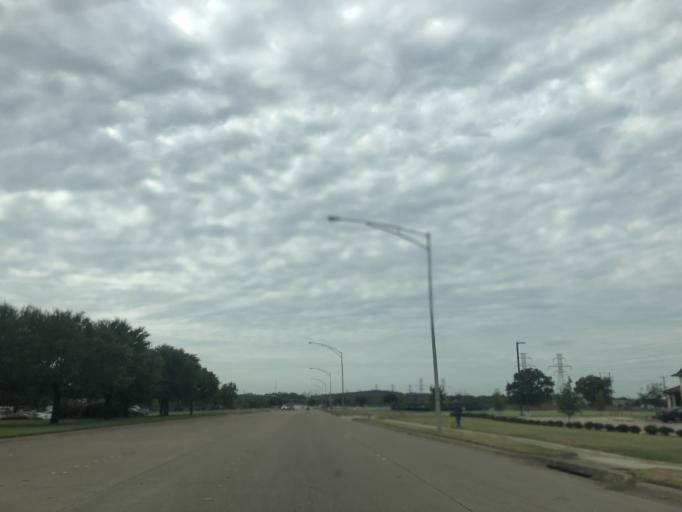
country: US
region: Texas
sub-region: Tarrant County
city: Richland Hills
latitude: 32.7889
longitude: -97.2213
